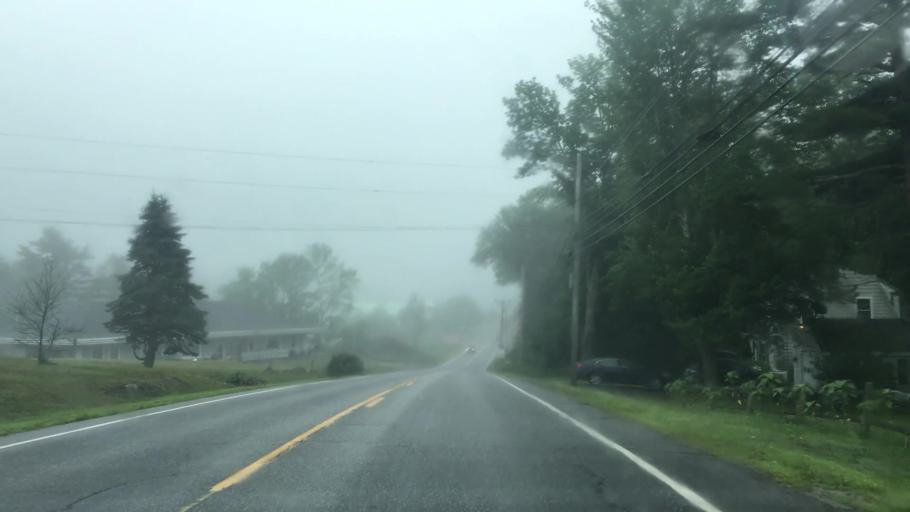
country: US
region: Maine
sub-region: Lincoln County
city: Boothbay
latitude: 43.8689
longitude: -69.6304
